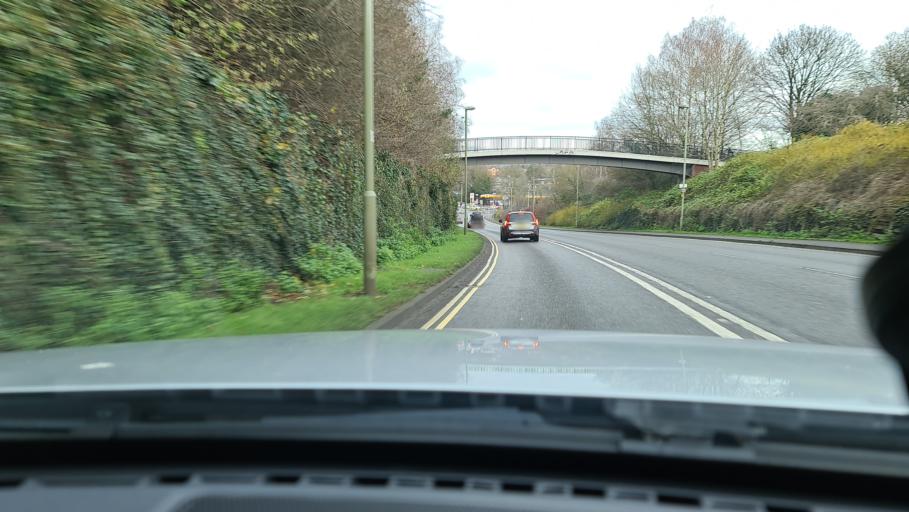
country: GB
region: England
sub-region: Oxfordshire
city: Banbury
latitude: 52.0563
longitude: -1.3346
